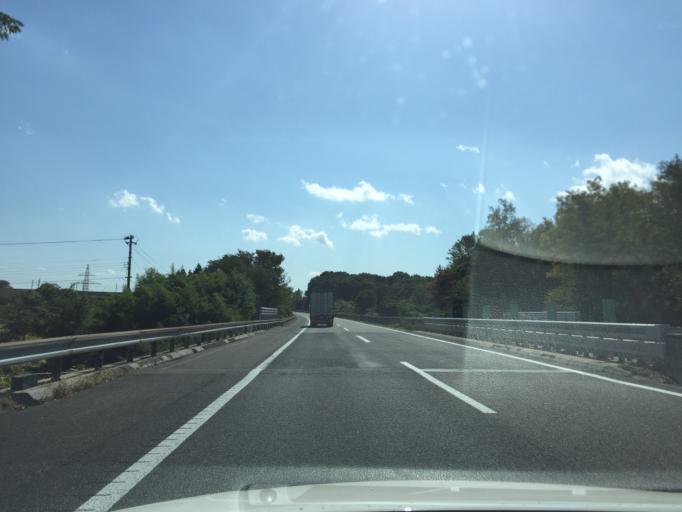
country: JP
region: Fukushima
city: Sukagawa
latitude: 37.3144
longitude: 140.3436
